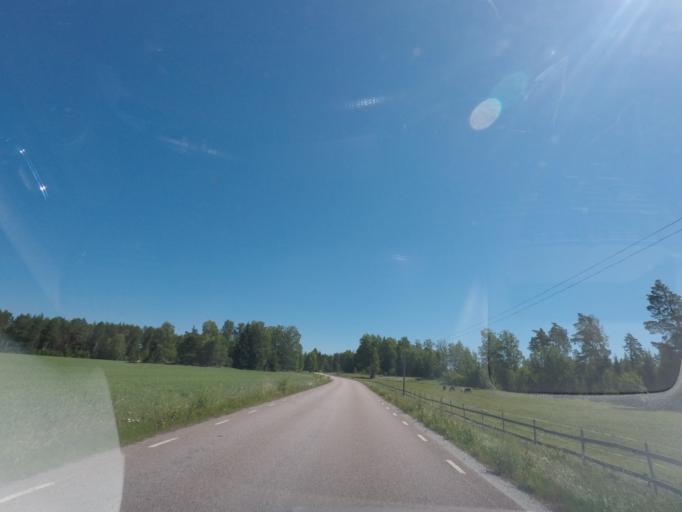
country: SE
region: Uppsala
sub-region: Enkopings Kommun
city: Irsta
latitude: 59.6815
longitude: 16.7891
